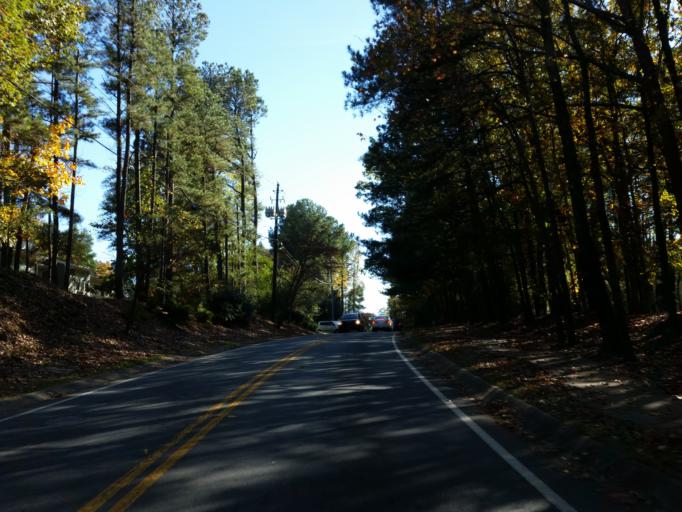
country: US
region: Georgia
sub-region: Cobb County
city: Smyrna
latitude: 33.9208
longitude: -84.4762
